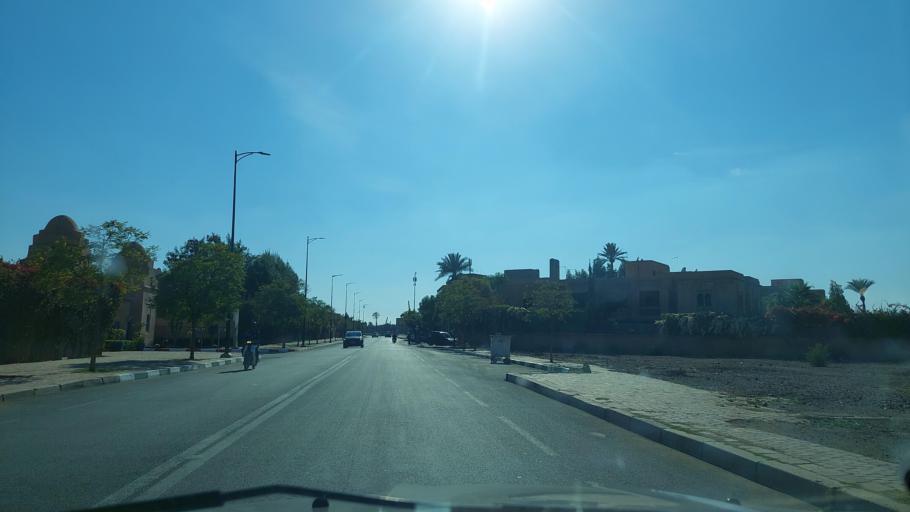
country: MA
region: Marrakech-Tensift-Al Haouz
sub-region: Marrakech
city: Marrakesh
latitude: 31.6603
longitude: -8.0632
